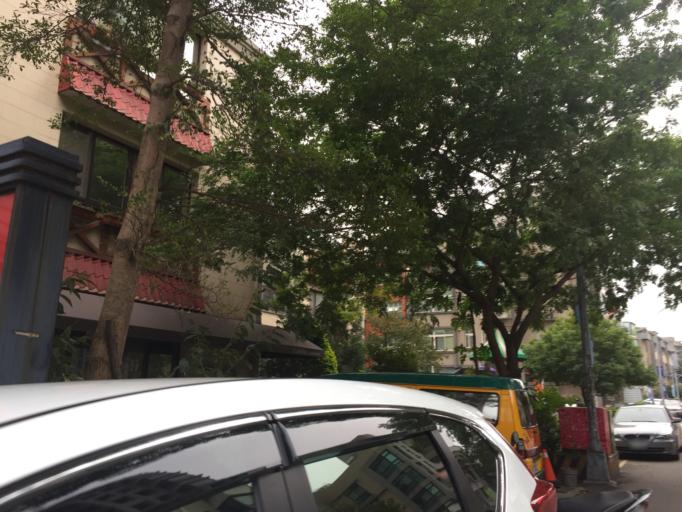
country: TW
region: Taiwan
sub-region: Hsinchu
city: Zhubei
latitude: 24.8197
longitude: 121.0255
